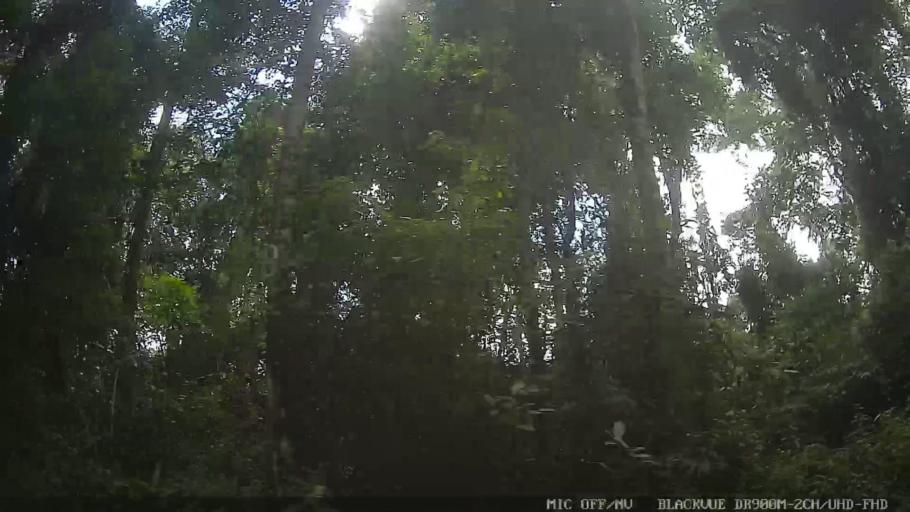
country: BR
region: Sao Paulo
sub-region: Atibaia
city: Atibaia
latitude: -23.1461
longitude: -46.6420
